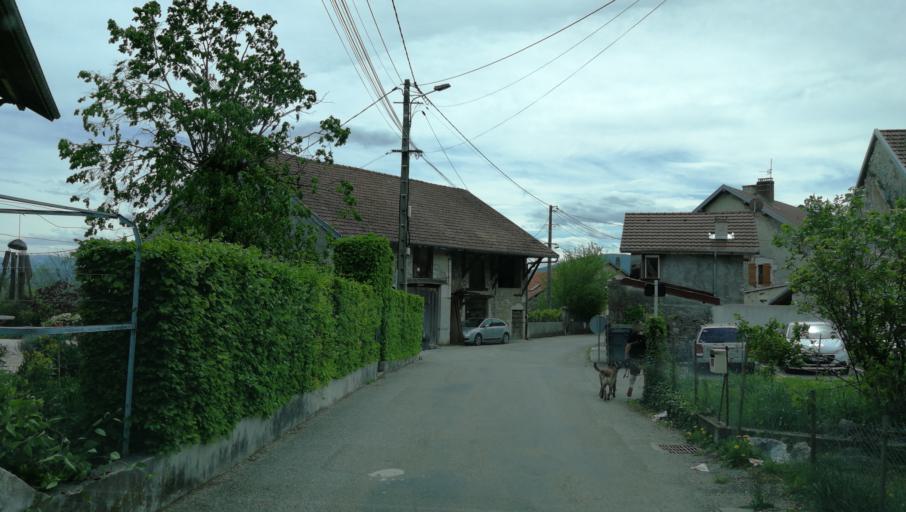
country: FR
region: Rhone-Alpes
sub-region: Departement de l'Ain
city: Bellegarde-sur-Valserine
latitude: 46.0071
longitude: 5.7840
